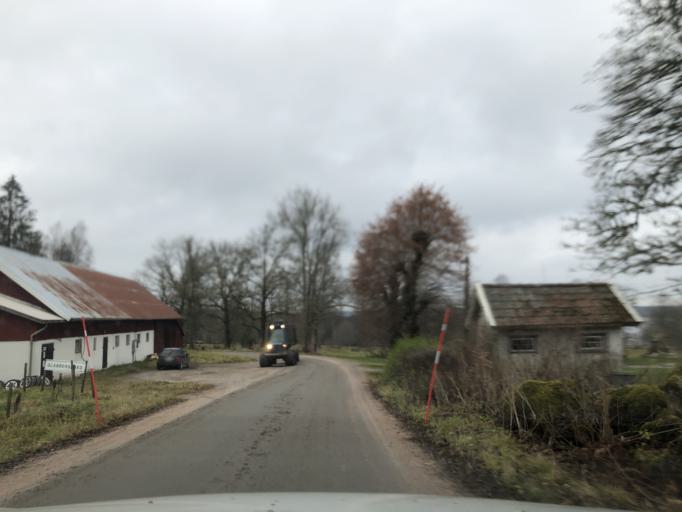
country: SE
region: Vaestra Goetaland
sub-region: Ulricehamns Kommun
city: Ulricehamn
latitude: 57.8513
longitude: 13.6342
